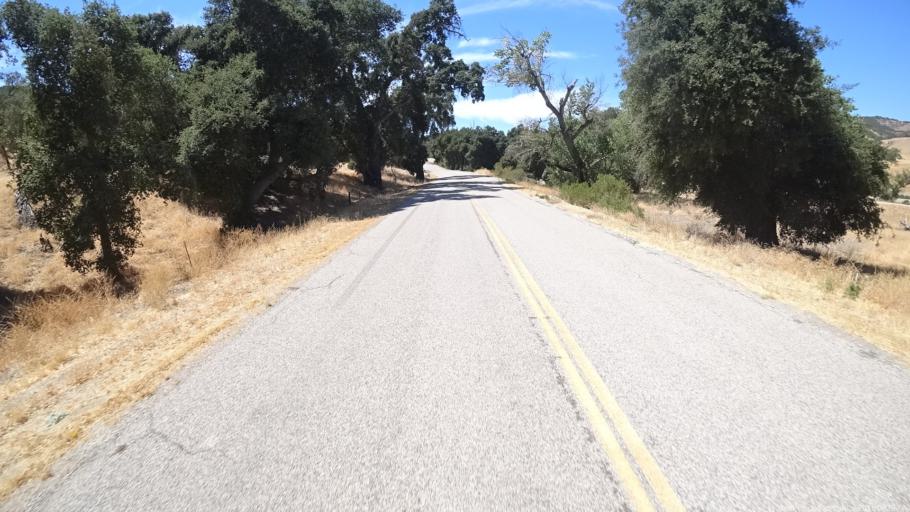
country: US
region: California
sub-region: San Luis Obispo County
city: Lake Nacimiento
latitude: 35.7938
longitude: -120.8624
